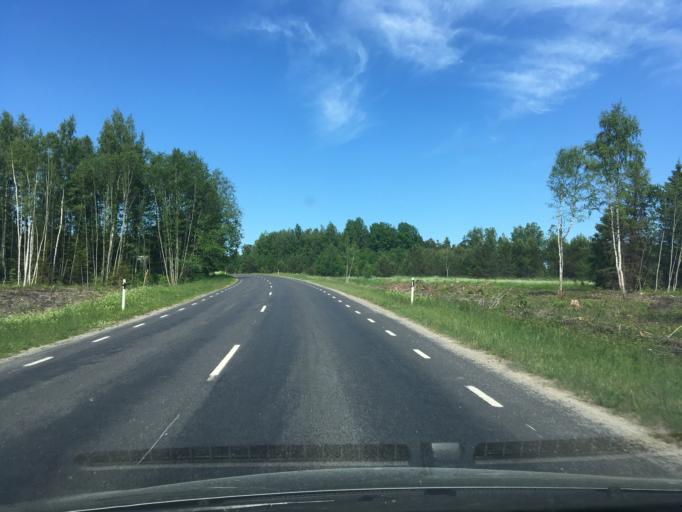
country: EE
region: Harju
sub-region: Raasiku vald
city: Raasiku
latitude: 59.1426
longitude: 25.2023
